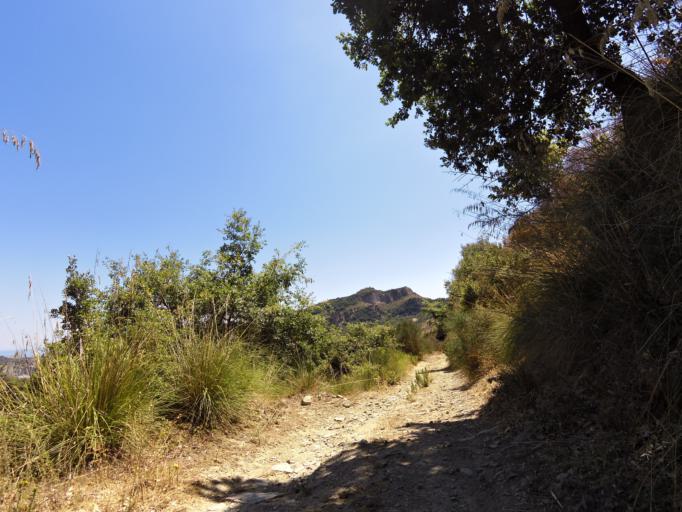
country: IT
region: Calabria
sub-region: Provincia di Reggio Calabria
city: Stilo
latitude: 38.4620
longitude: 16.4617
